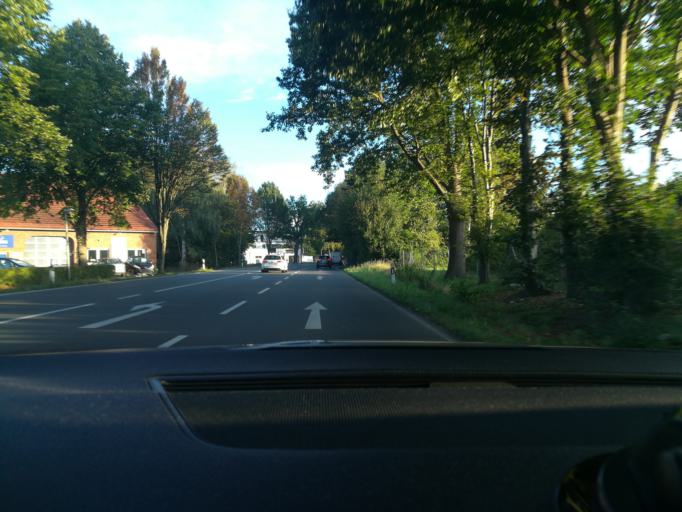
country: DE
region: North Rhine-Westphalia
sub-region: Regierungsbezirk Detmold
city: Minden
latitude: 52.3160
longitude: 8.8802
